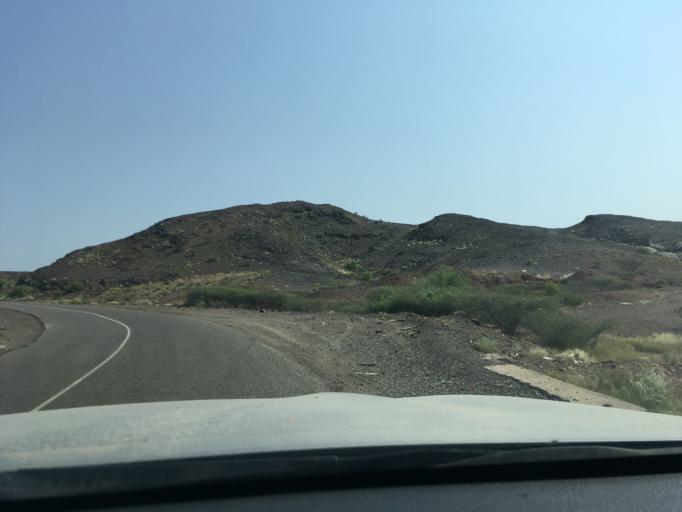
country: YE
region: Lahij
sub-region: Al Milah
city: Al Milah
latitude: 13.3804
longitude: 44.8088
